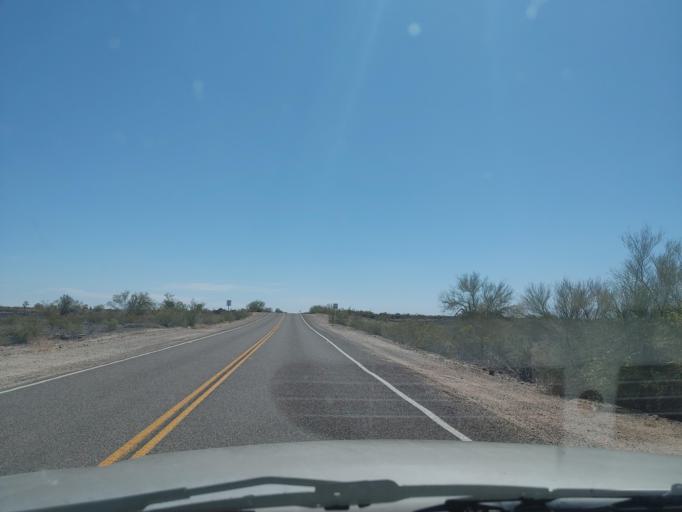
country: US
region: Arizona
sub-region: Maricopa County
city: Gila Bend
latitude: 32.8916
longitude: -113.2427
